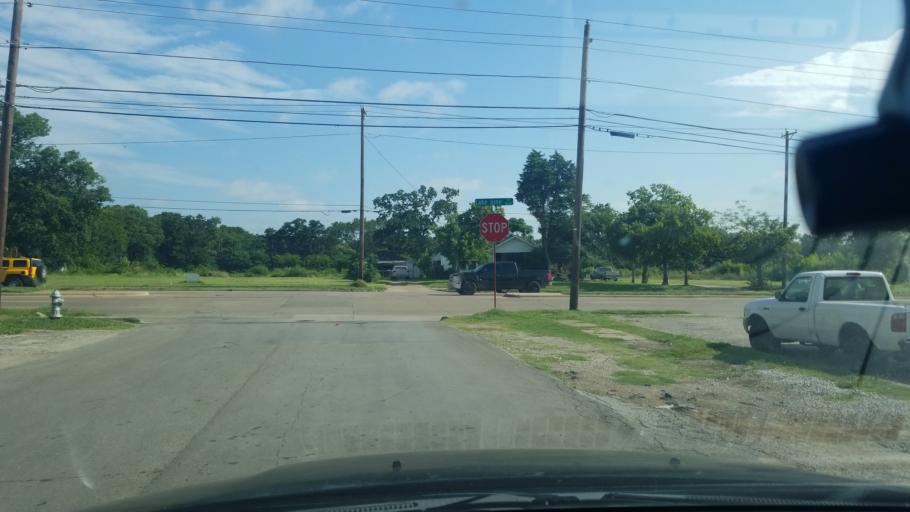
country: US
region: Texas
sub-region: Dallas County
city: Balch Springs
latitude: 32.7338
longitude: -96.6733
